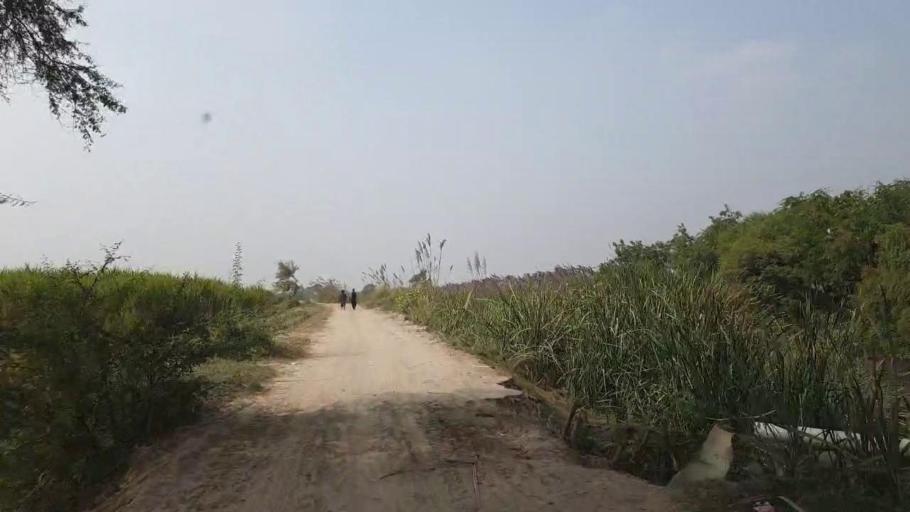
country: PK
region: Sindh
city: Matli
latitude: 25.0327
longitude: 68.5932
